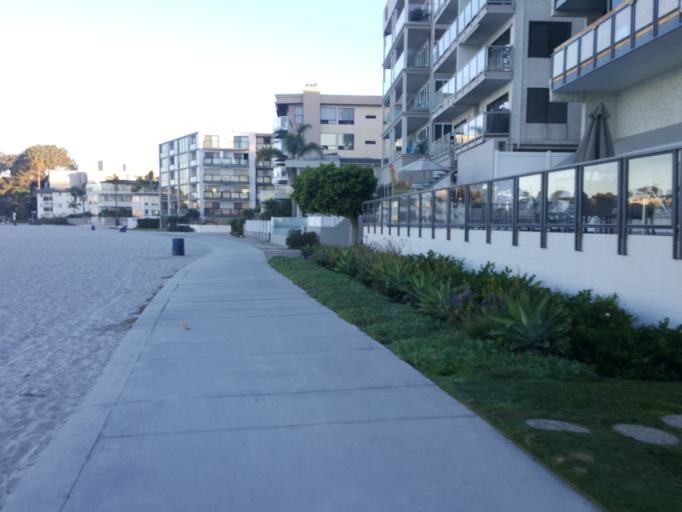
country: US
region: California
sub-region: San Diego County
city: La Jolla
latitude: 32.7890
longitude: -117.2411
